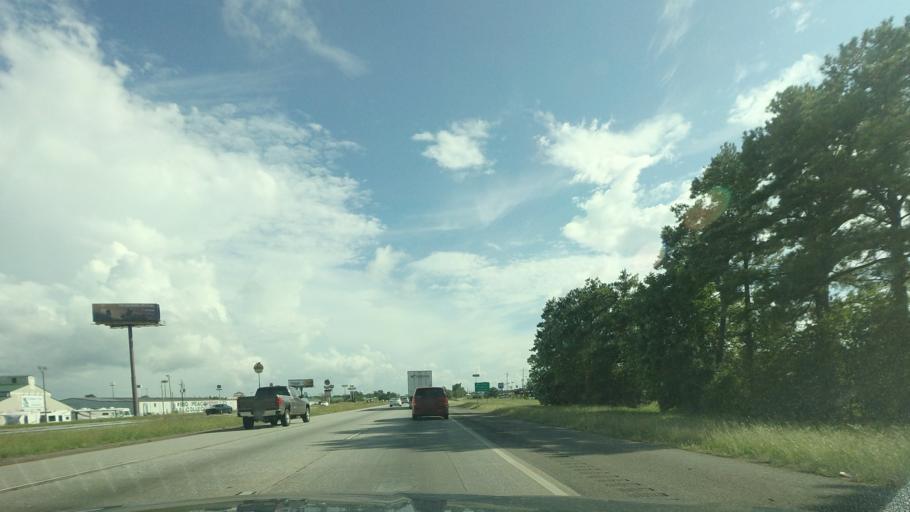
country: US
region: Georgia
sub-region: Peach County
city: Byron
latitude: 32.6664
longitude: -83.7446
